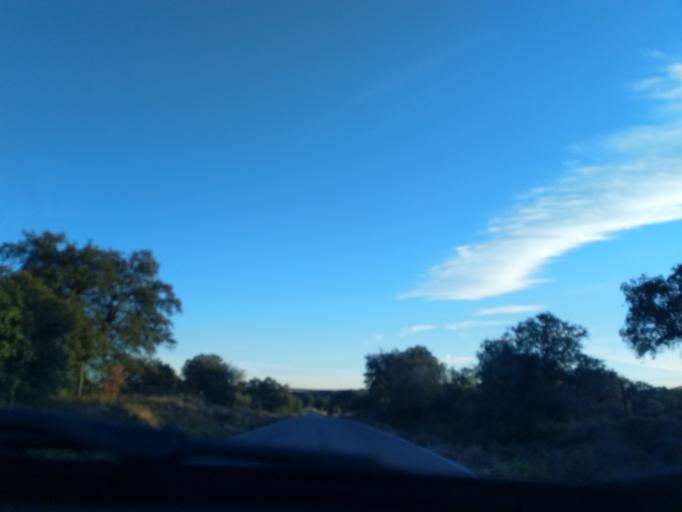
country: ES
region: Extremadura
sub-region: Provincia de Badajoz
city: Valverde de Llerena
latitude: 38.2414
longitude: -5.8247
